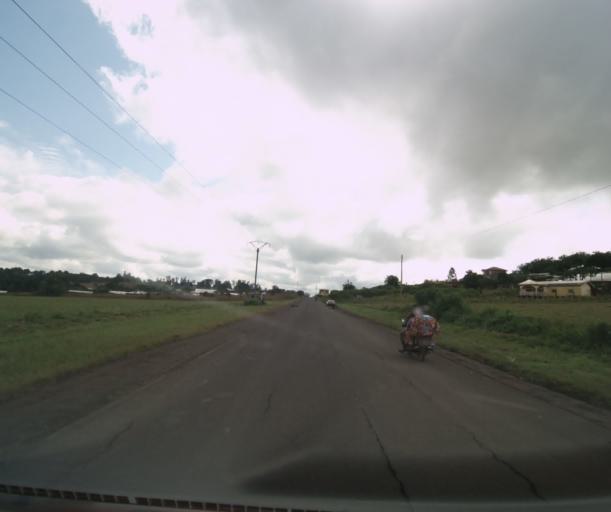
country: CM
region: West
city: Foumbot
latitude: 5.5004
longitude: 10.6169
